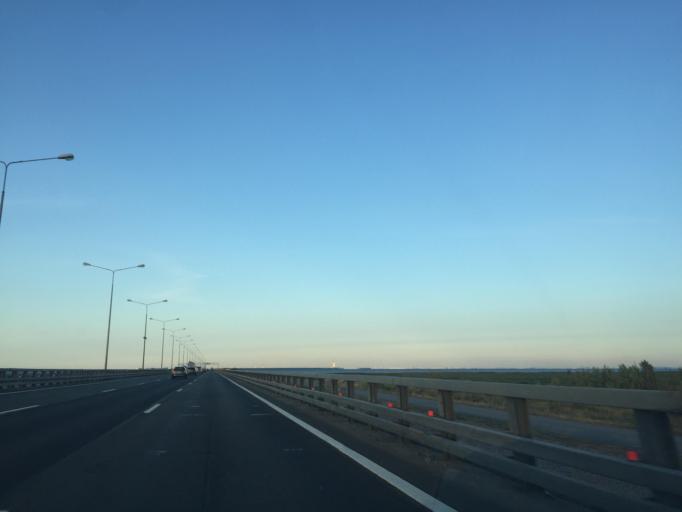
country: RU
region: St.-Petersburg
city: Kronshtadt
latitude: 60.0202
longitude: 29.7600
